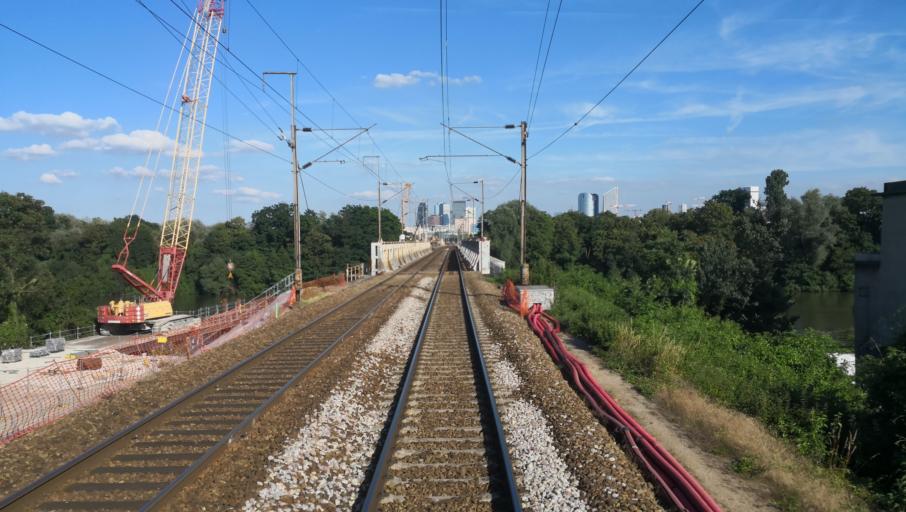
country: FR
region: Ile-de-France
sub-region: Departement des Yvelines
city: Houilles
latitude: 48.9124
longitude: 2.2017
